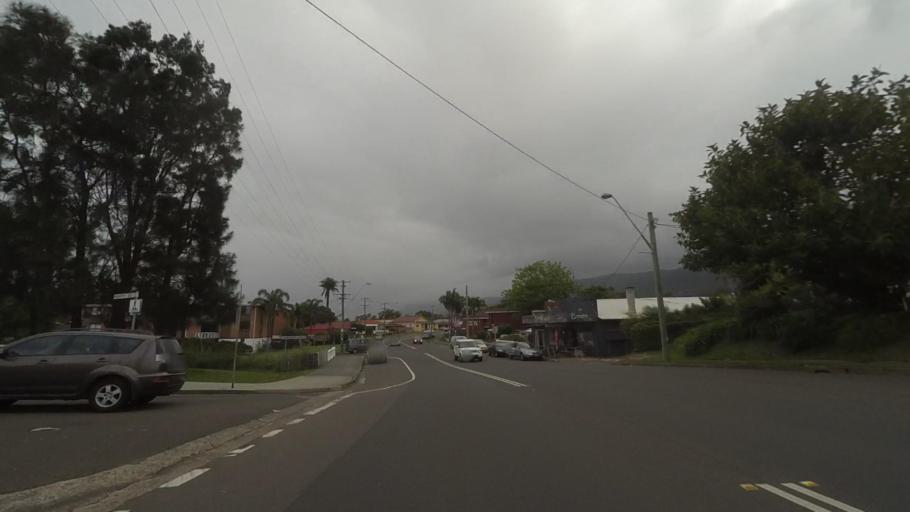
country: AU
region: New South Wales
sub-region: Wollongong
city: Bulli
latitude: -34.3136
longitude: 150.9270
